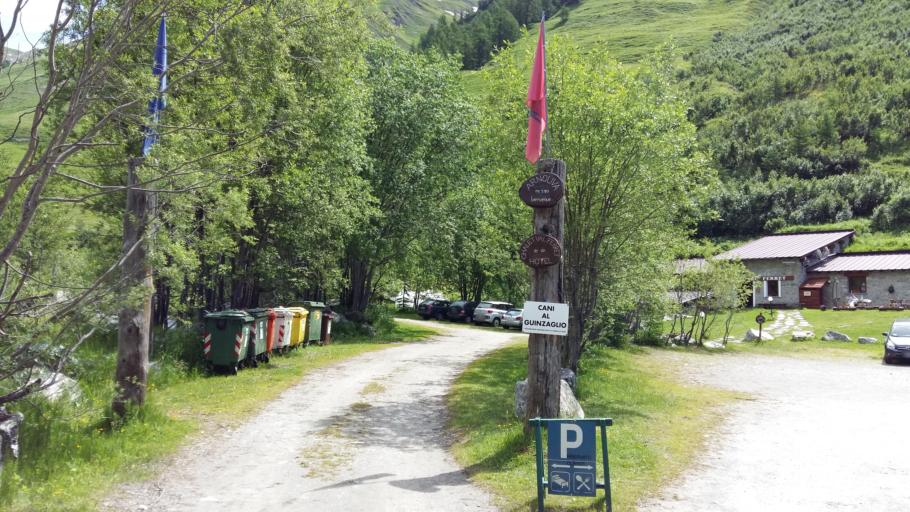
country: IT
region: Aosta Valley
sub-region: Valle d'Aosta
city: Courmayeur
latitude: 45.8712
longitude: 7.0529
